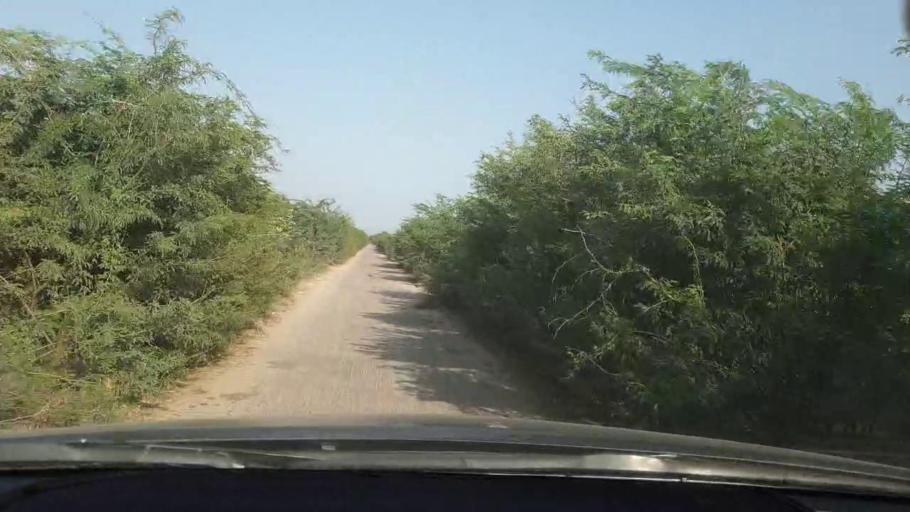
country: PK
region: Sindh
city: Naukot
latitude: 24.7666
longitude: 69.2432
